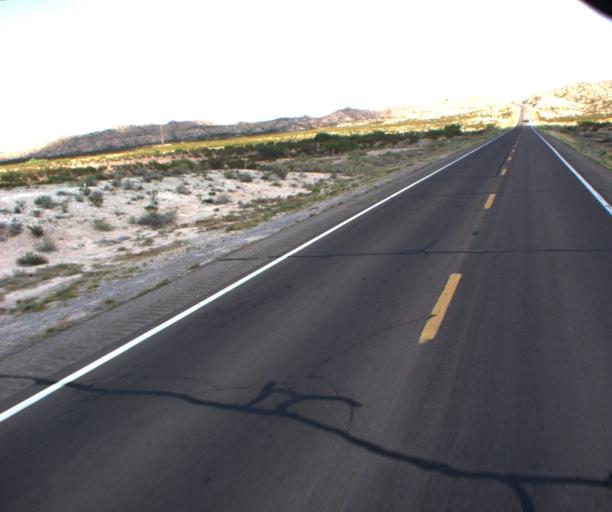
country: US
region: Arizona
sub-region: Greenlee County
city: Clifton
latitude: 32.7609
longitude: -109.1396
